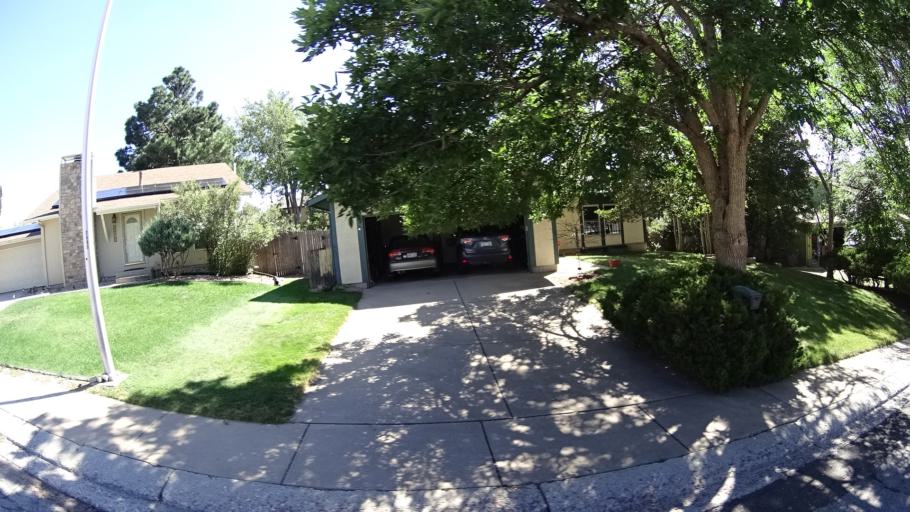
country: US
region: Colorado
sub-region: El Paso County
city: Cimarron Hills
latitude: 38.8755
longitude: -104.7302
